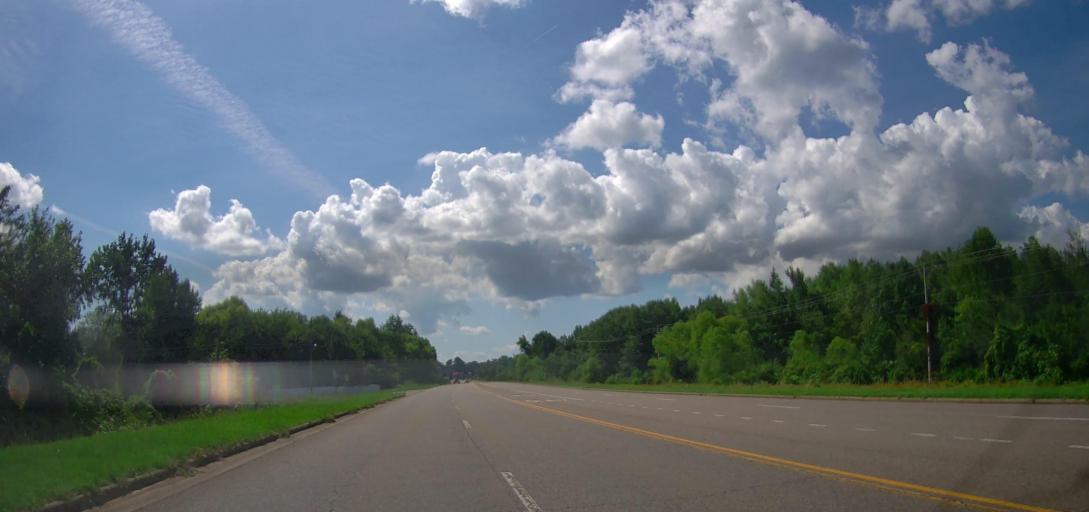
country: US
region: Alabama
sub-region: Pickens County
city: Reform
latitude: 33.3746
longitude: -88.0053
